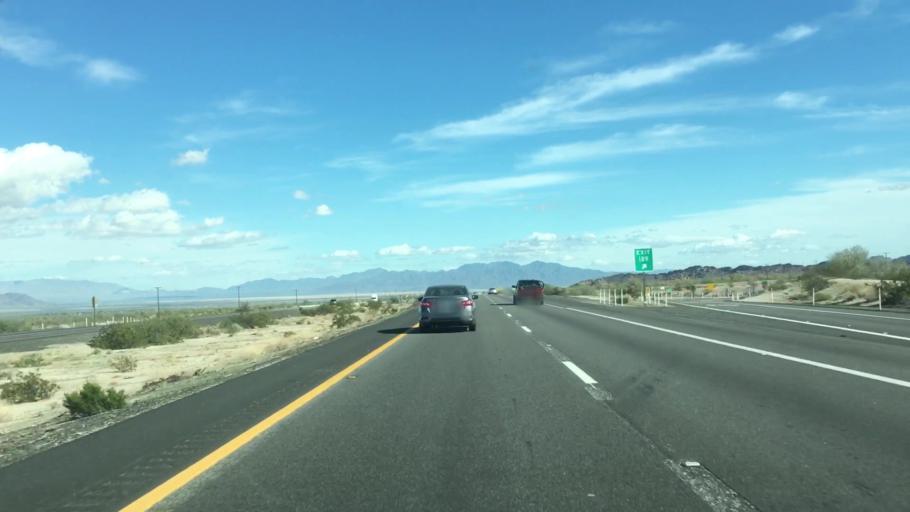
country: US
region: California
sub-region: Imperial County
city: Niland
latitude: 33.7014
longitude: -115.4548
